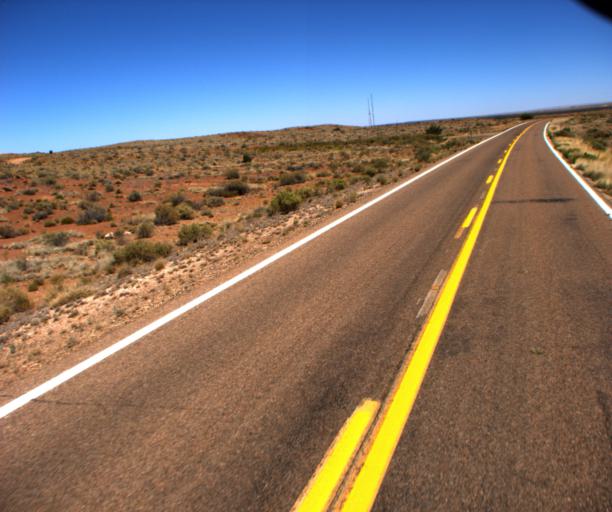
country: US
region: Arizona
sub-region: Navajo County
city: Winslow
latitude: 34.9579
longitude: -110.6473
